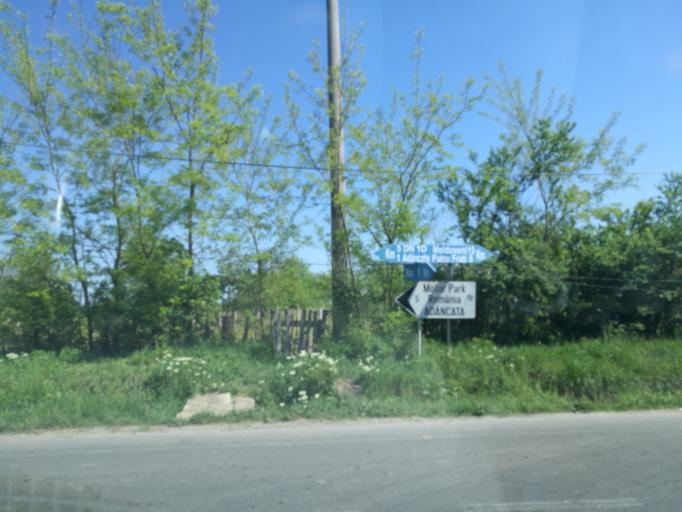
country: RO
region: Ialomita
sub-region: Comuna Adancata
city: Adancata
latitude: 44.7617
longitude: 26.4471
